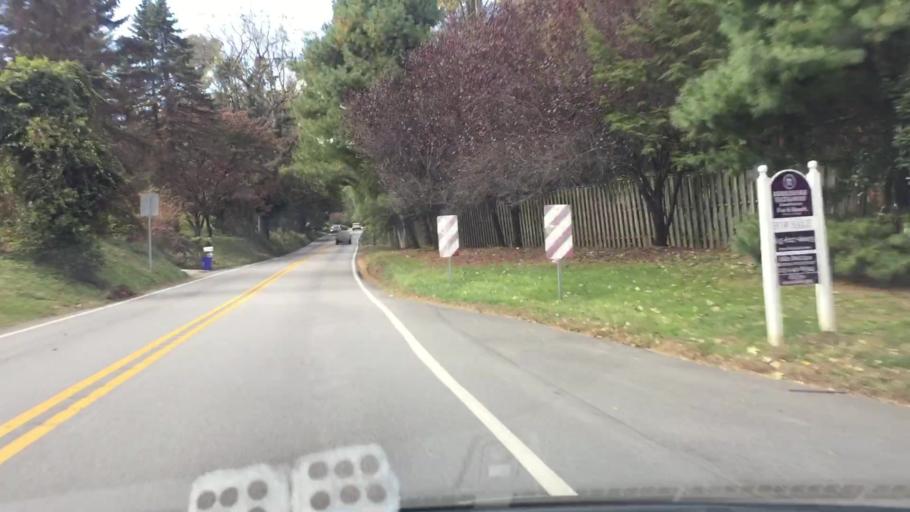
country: US
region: Pennsylvania
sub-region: Delaware County
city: Lima
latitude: 39.9556
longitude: -75.4245
